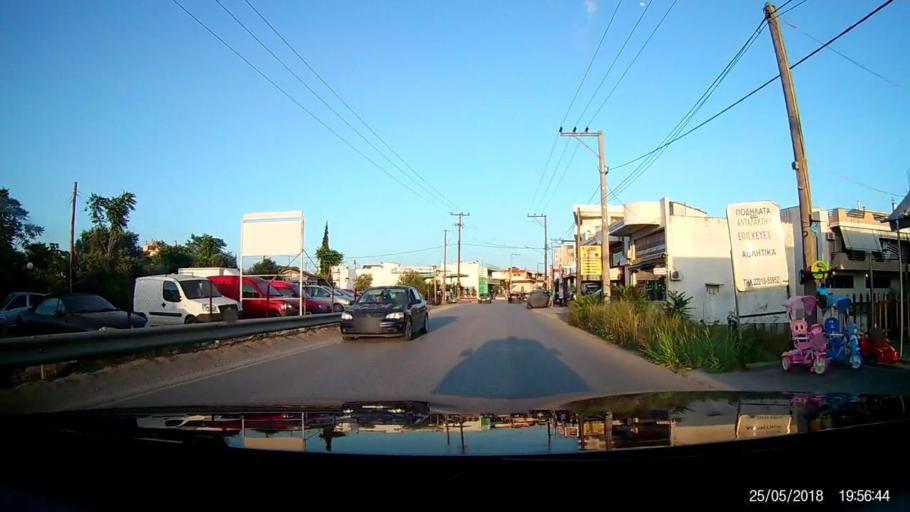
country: GR
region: Central Greece
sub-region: Nomos Evvoias
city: Vasilikon
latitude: 38.4277
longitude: 23.6639
